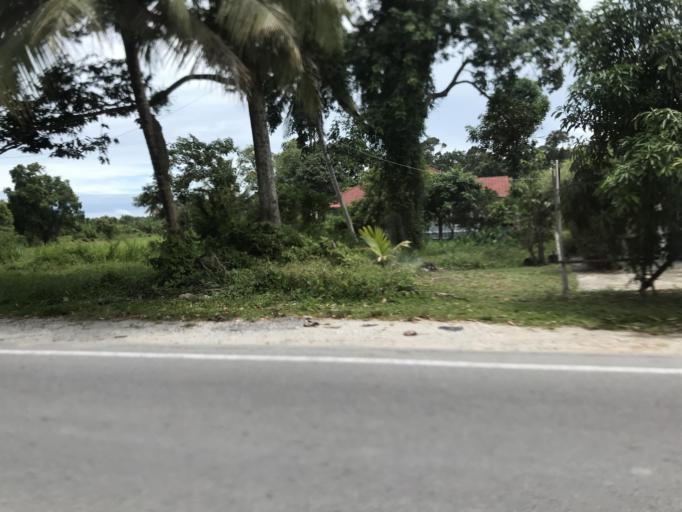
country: MY
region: Kelantan
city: Tumpat
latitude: 6.1686
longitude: 102.1908
